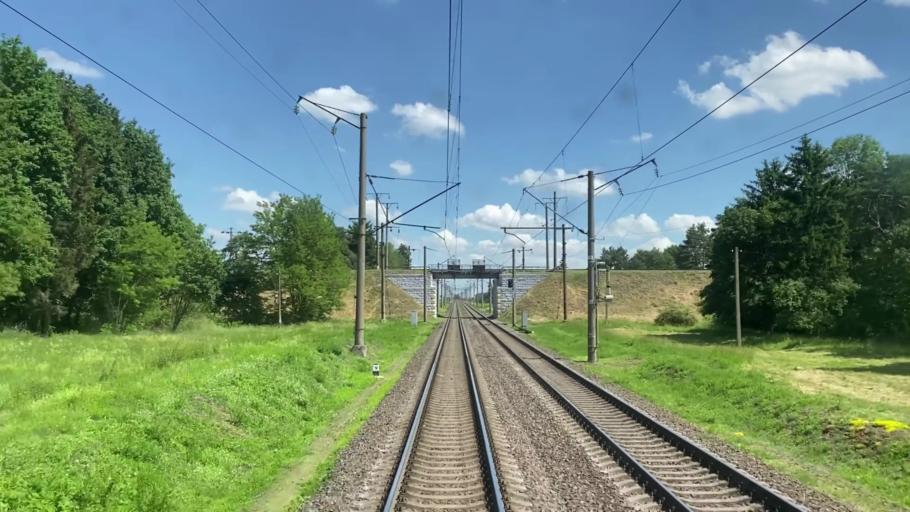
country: BY
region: Brest
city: Baranovichi
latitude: 53.0940
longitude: 25.9406
